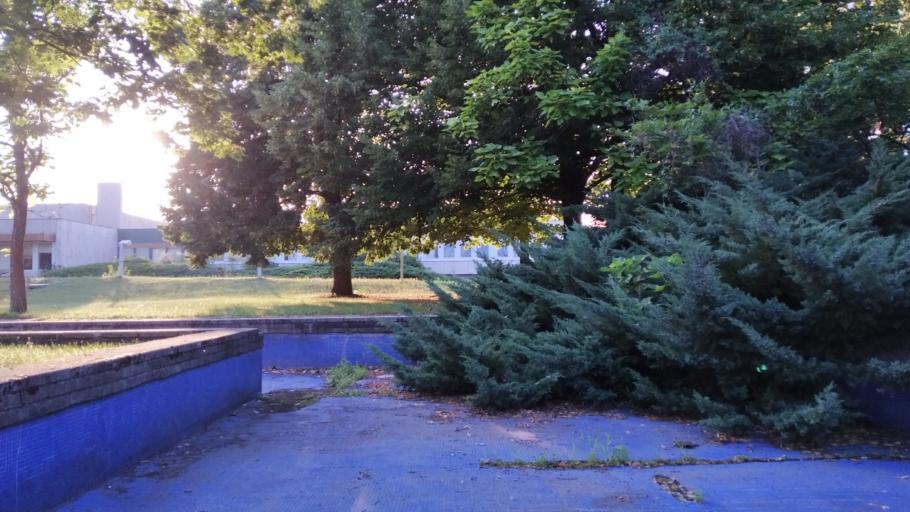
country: HU
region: Budapest
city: Budapest XIX. keruelet
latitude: 47.4252
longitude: 19.1339
